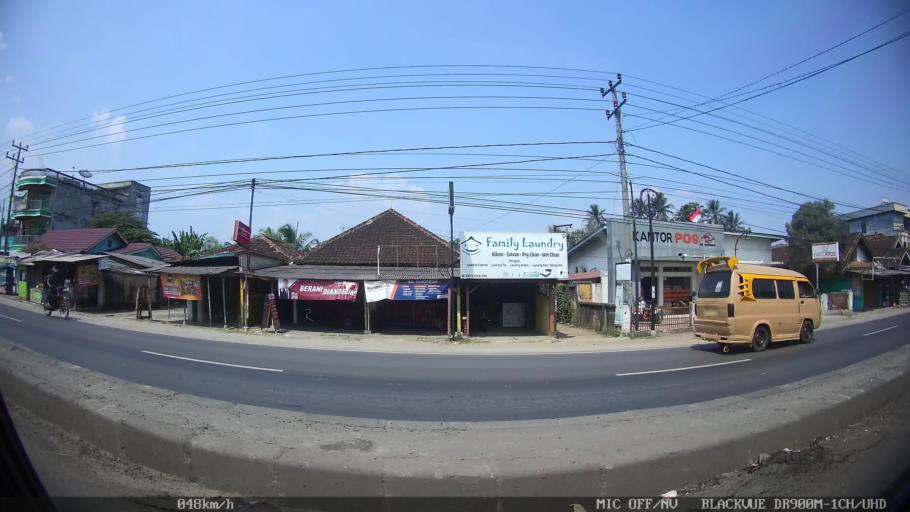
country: ID
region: Lampung
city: Natar
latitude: -5.3143
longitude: 105.1965
